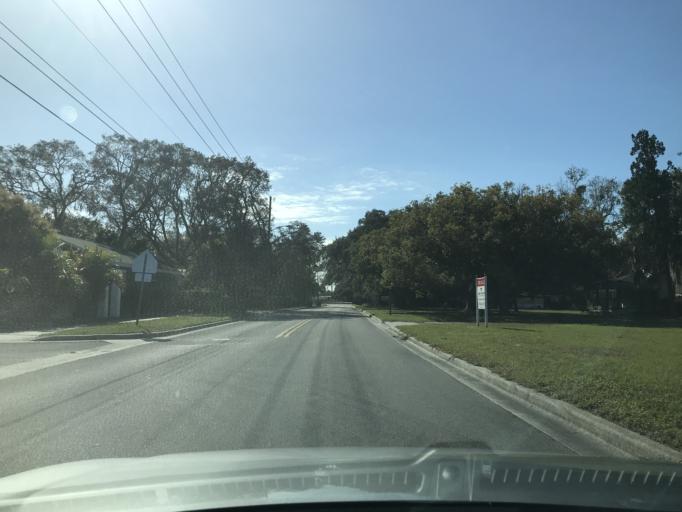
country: US
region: Florida
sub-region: Pinellas County
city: Belleair
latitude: 27.9335
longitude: -82.7916
